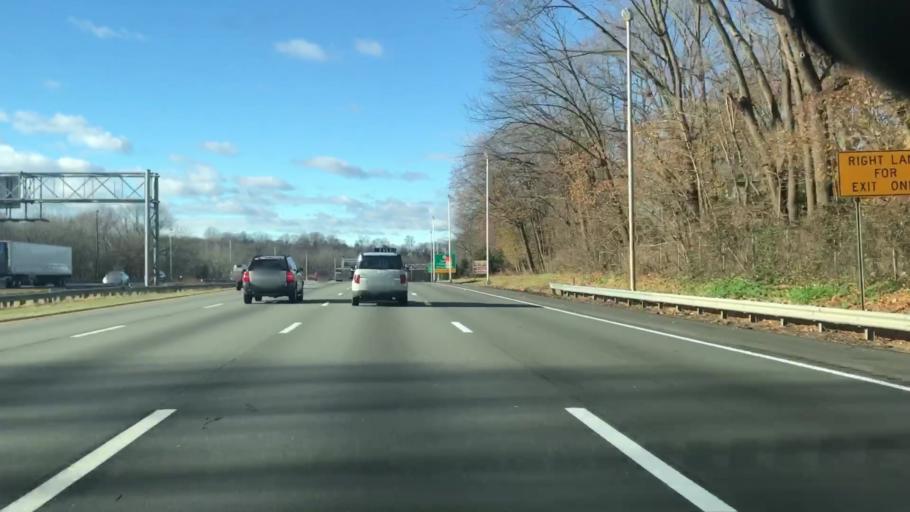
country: US
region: New Jersey
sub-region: Hunterdon County
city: Annandale
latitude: 40.6398
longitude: -74.8801
